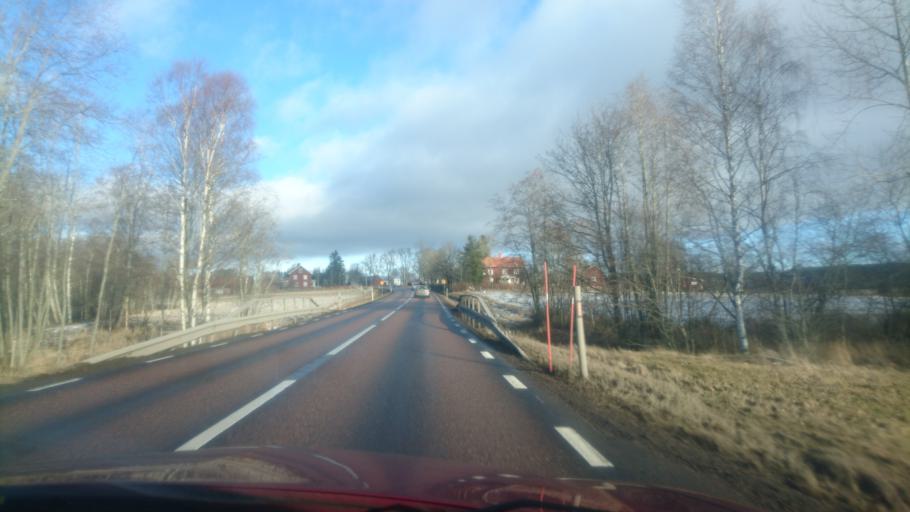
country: SE
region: Vaermland
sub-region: Sunne Kommun
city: Sunne
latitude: 59.6591
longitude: 13.1547
